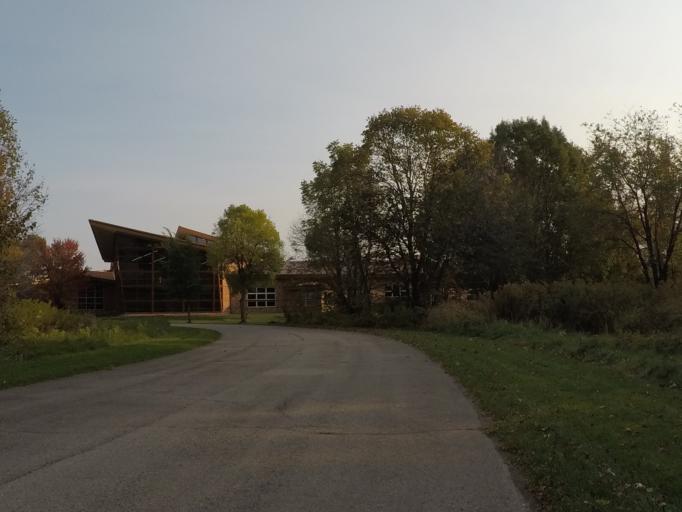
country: US
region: Wisconsin
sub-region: Dane County
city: Verona
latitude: 42.9983
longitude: -89.5284
